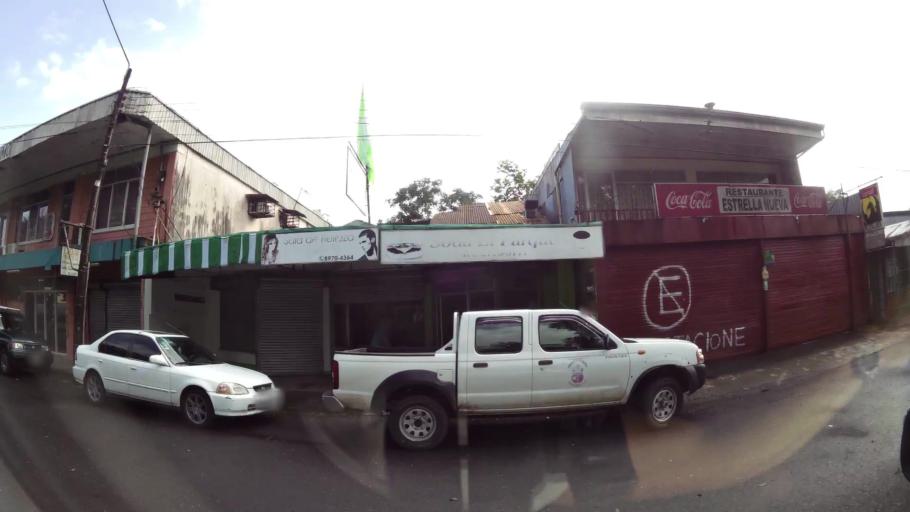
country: CR
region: Limon
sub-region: Canton de Guacimo
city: Guacimo
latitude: 10.2086
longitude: -83.6819
